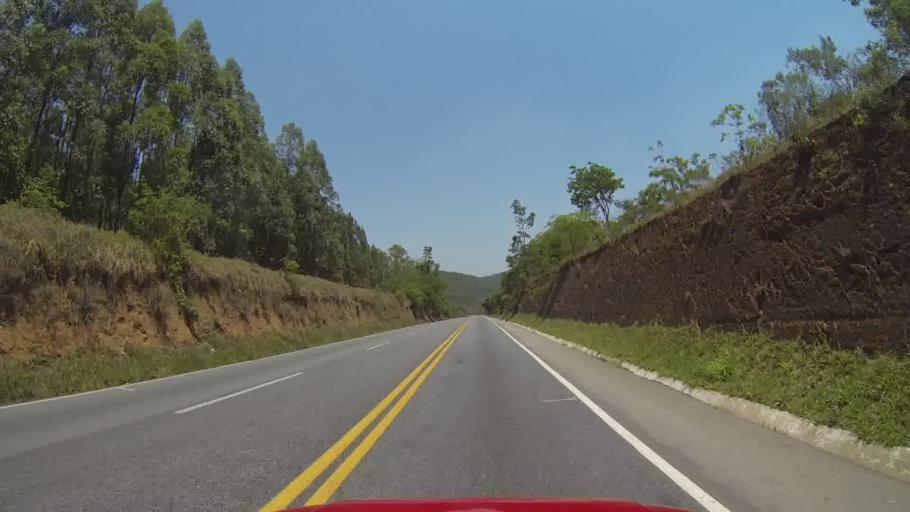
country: BR
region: Minas Gerais
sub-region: Itapecerica
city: Itapecerica
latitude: -20.2814
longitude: -45.1409
